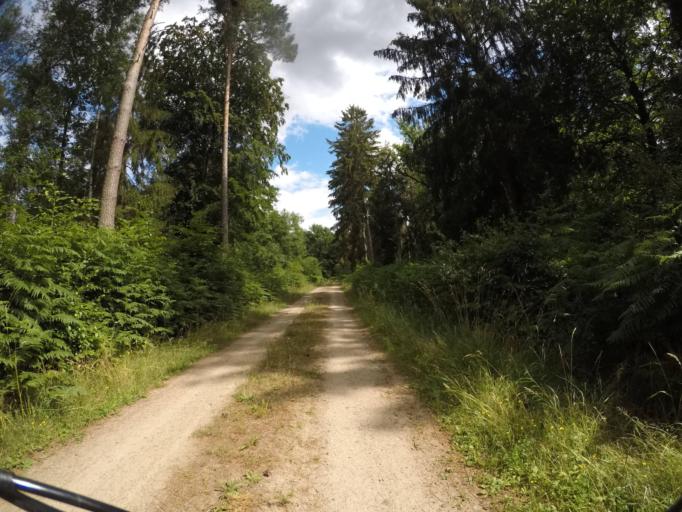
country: DE
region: Mecklenburg-Vorpommern
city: Lubtheen
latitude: 53.2772
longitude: 10.9906
